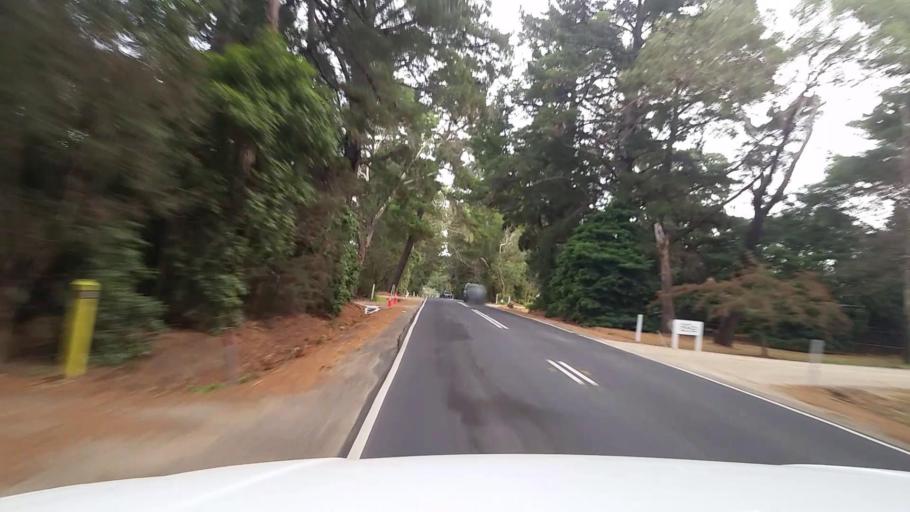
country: AU
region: Victoria
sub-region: Mornington Peninsula
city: Balnarring
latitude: -38.3667
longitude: 145.1198
